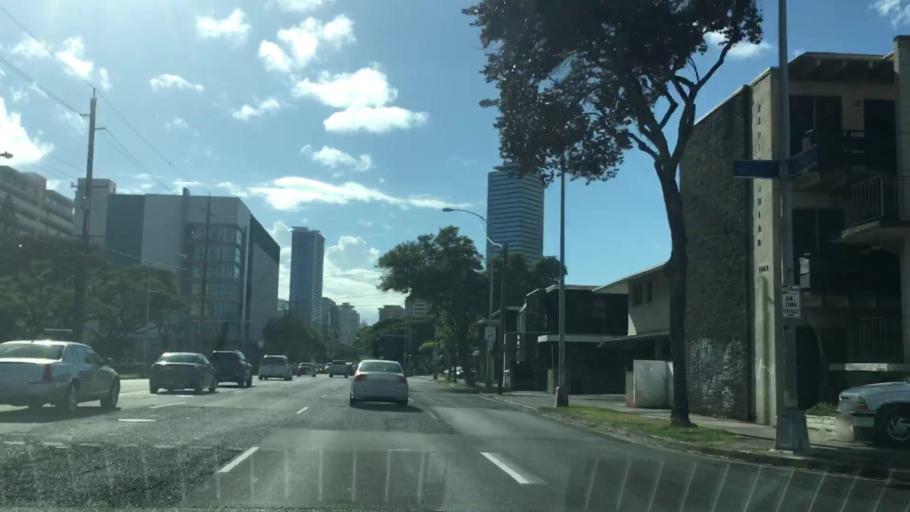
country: US
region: Hawaii
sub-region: Honolulu County
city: Honolulu
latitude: 21.2892
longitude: -157.8312
